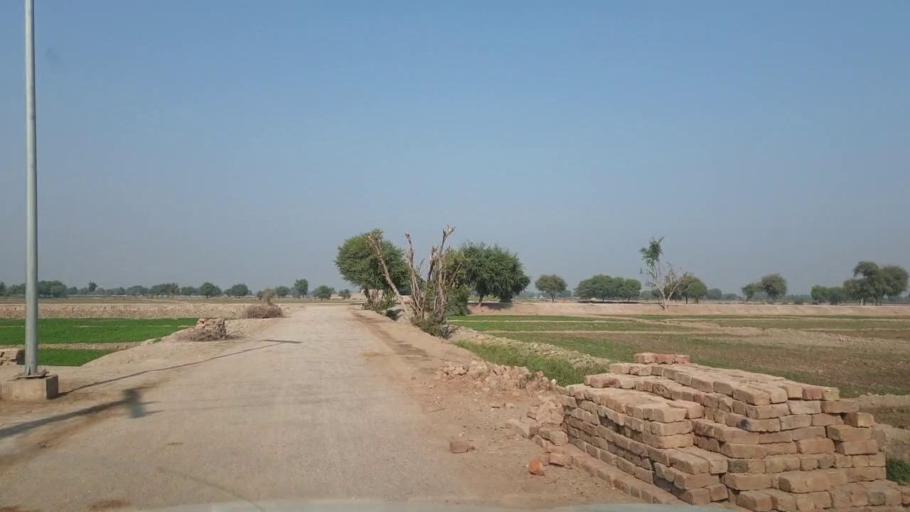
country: PK
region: Sindh
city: Bhan
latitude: 26.5087
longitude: 67.7939
